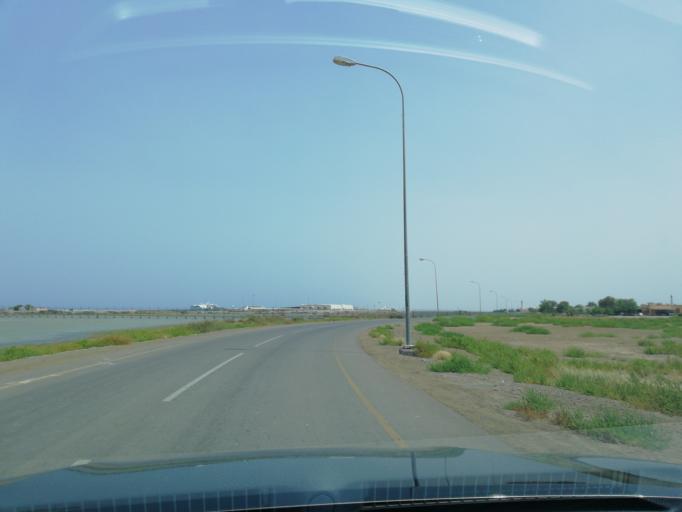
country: OM
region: Al Batinah
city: Shinas
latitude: 24.7532
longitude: 56.4670
